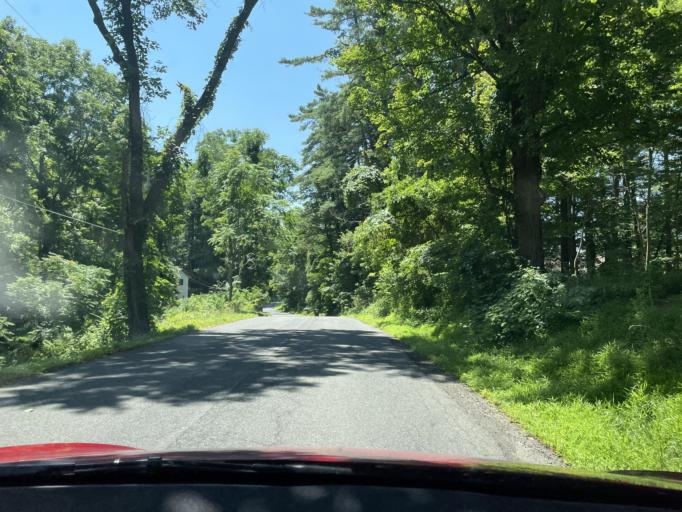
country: US
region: New York
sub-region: Ulster County
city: Glasco
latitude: 42.0282
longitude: -73.9730
